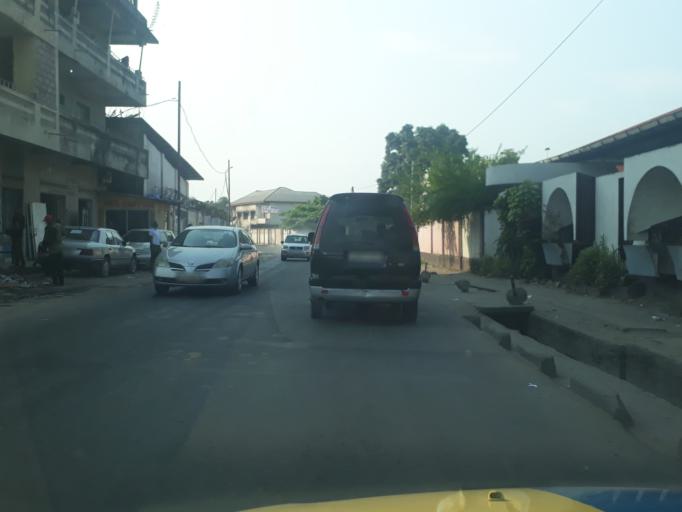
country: CD
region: Kinshasa
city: Kinshasa
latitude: -4.3126
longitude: 15.3304
